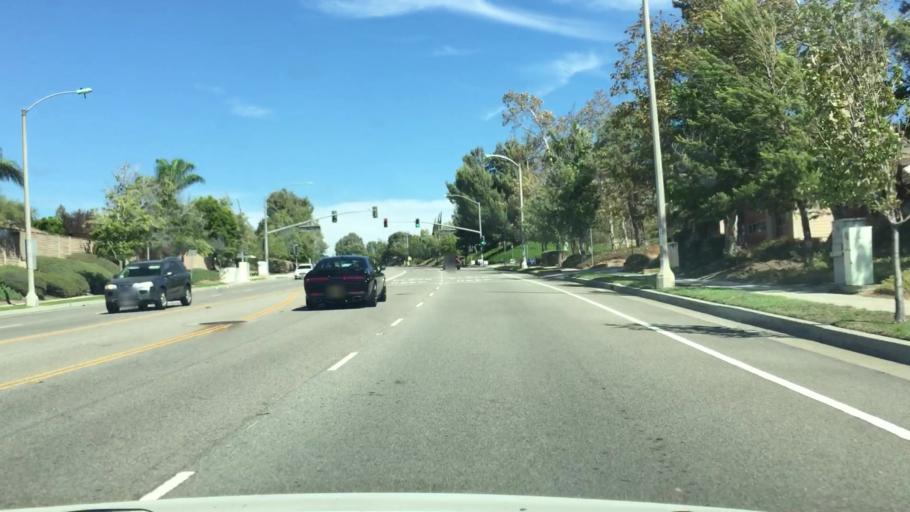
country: US
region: California
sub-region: Riverside County
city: Corona
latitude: 33.8762
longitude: -117.6361
